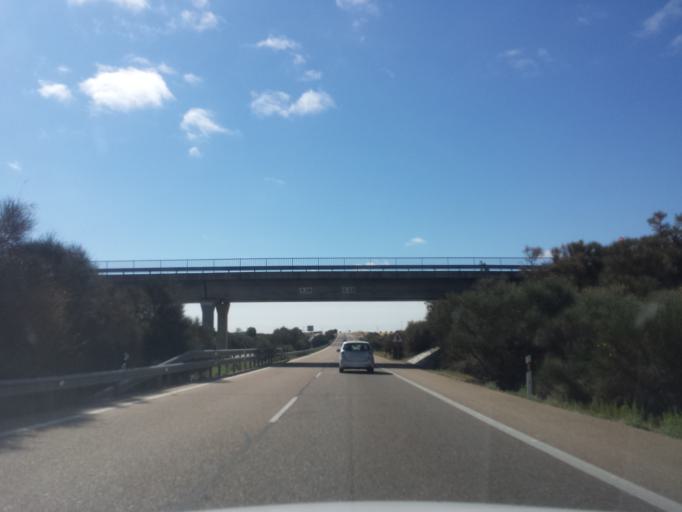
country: ES
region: Castille and Leon
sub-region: Provincia de Valladolid
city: Uruena
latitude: 41.6792
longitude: -5.2075
